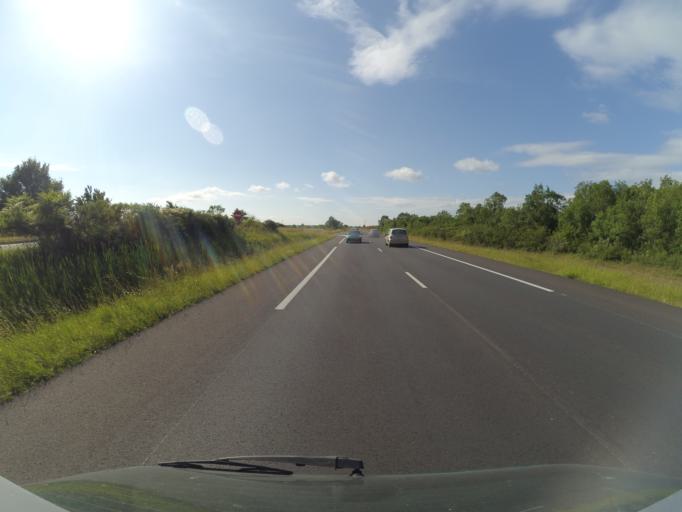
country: FR
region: Poitou-Charentes
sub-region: Departement de la Charente-Maritime
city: Saint-Agnant
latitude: 45.8458
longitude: -0.9521
